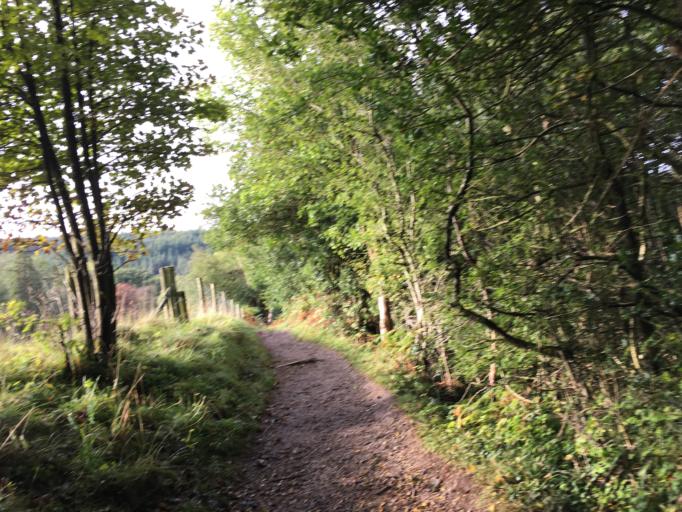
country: GB
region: England
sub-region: North Yorkshire
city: Sleights
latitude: 54.3979
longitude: -0.7287
